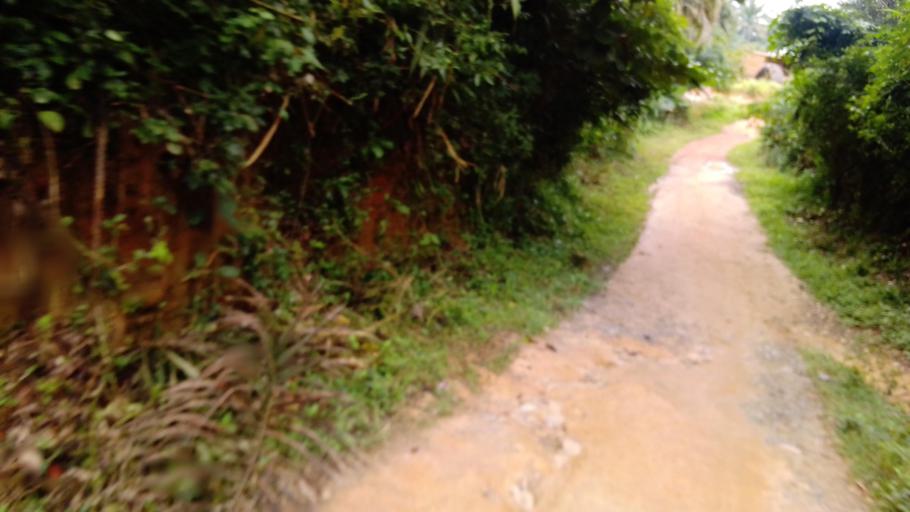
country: SL
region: Eastern Province
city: Koidu
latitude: 8.6589
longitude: -10.9350
